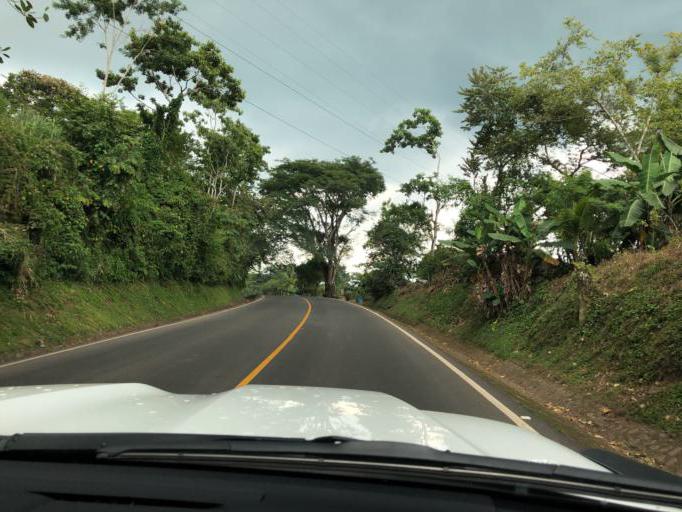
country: NI
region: Chontales
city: Villa Sandino
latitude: 11.9909
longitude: -84.8256
